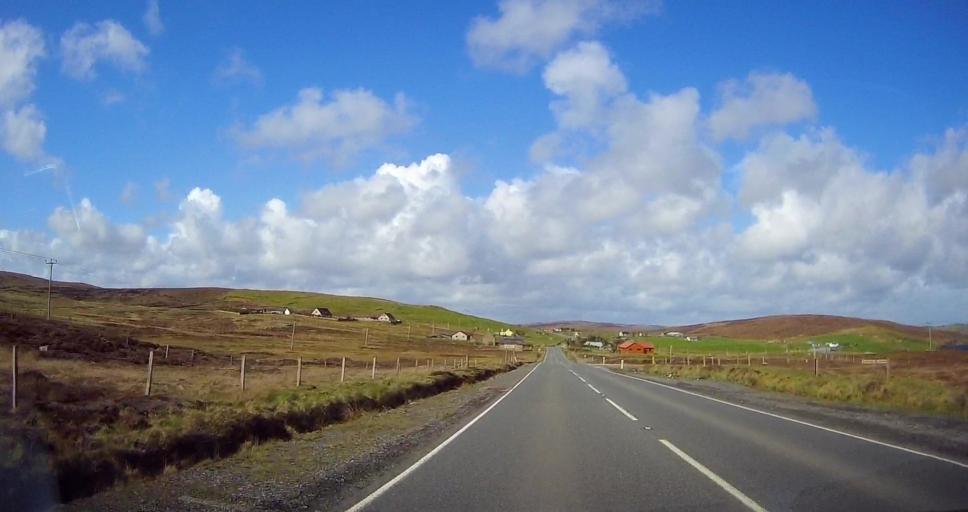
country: GB
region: Scotland
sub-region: Shetland Islands
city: Lerwick
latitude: 60.2321
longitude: -1.2358
